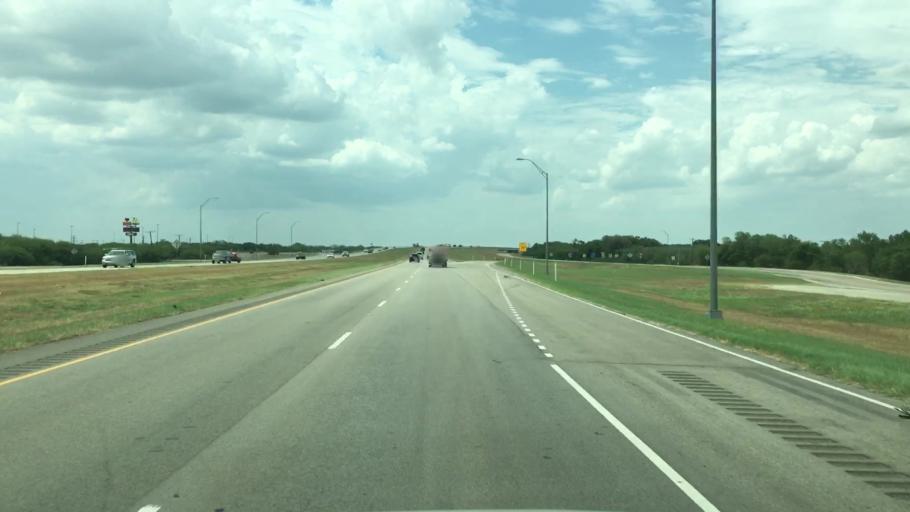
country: US
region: Texas
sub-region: Live Oak County
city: Three Rivers
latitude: 28.5191
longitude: -98.1789
